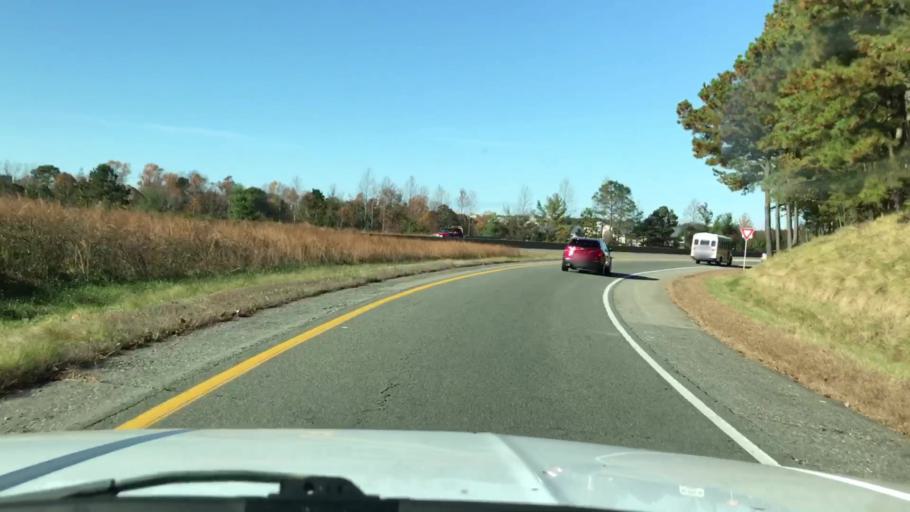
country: US
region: Virginia
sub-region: Henrico County
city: Short Pump
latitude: 37.6372
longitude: -77.5725
